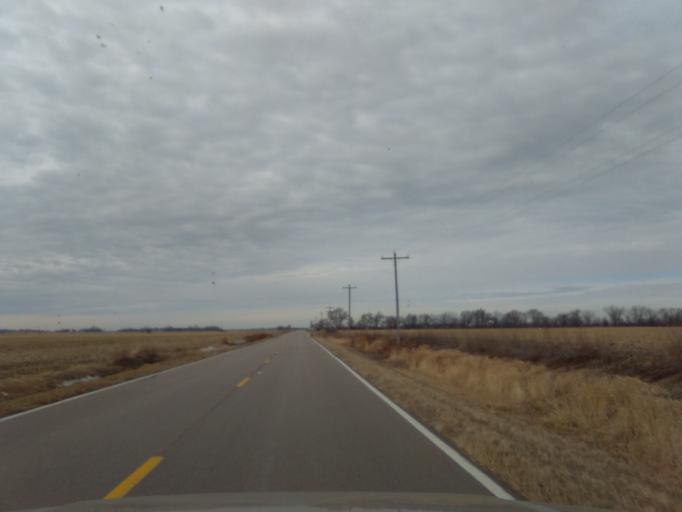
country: US
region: Nebraska
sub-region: Hall County
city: Grand Island
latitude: 40.7711
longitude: -98.4285
